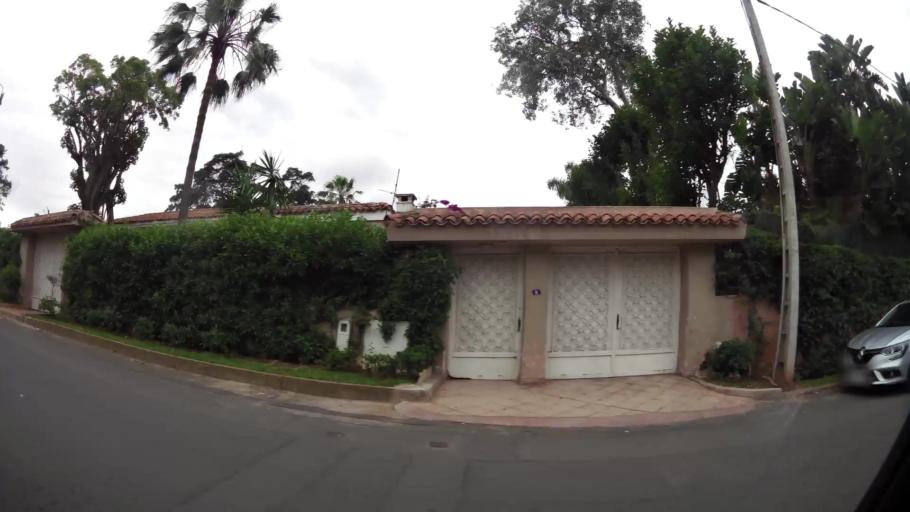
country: MA
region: Grand Casablanca
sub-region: Casablanca
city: Casablanca
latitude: 33.5880
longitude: -7.6531
